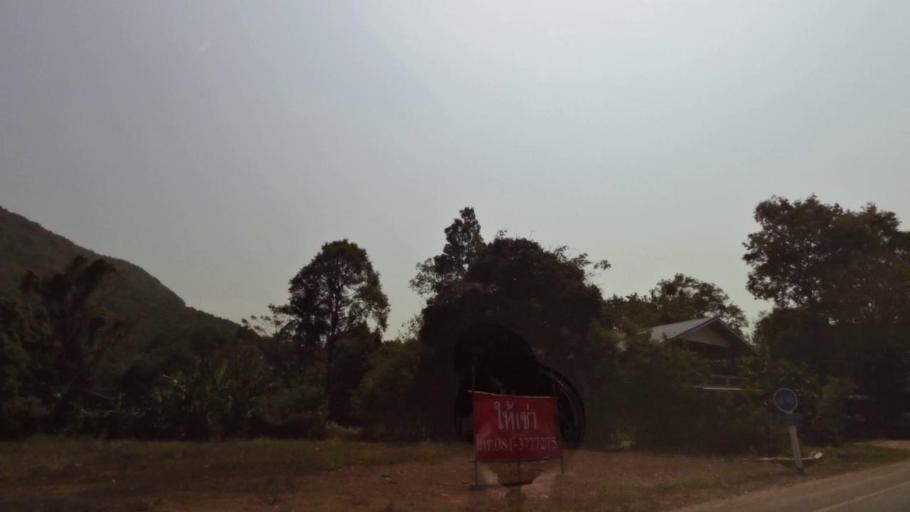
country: TH
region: Chanthaburi
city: Tha Mai
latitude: 12.5676
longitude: 101.9154
